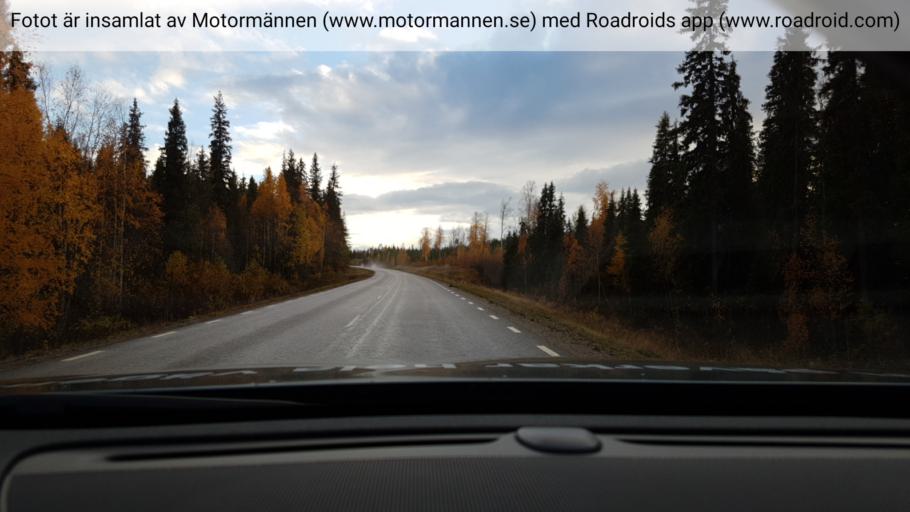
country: SE
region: Norrbotten
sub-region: Overkalix Kommun
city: OEverkalix
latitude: 66.7587
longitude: 22.6782
